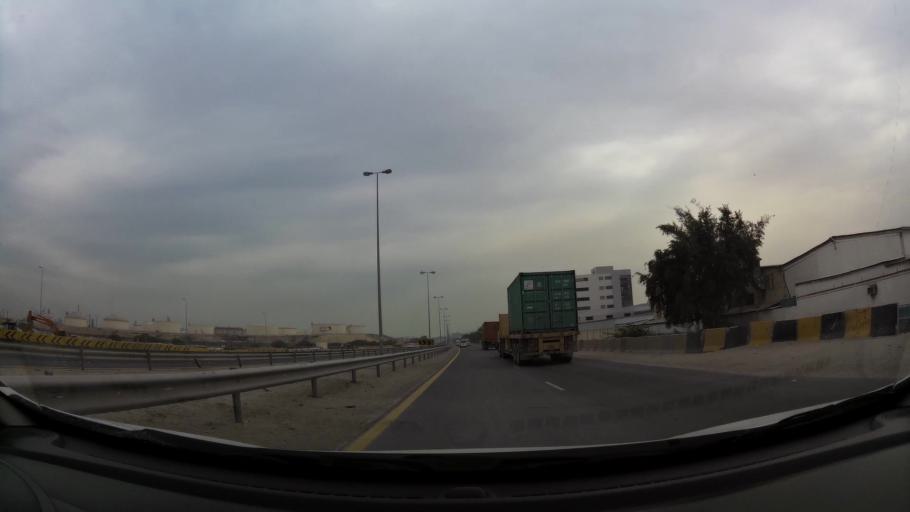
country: BH
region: Northern
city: Ar Rifa'
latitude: 26.1188
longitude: 50.5928
